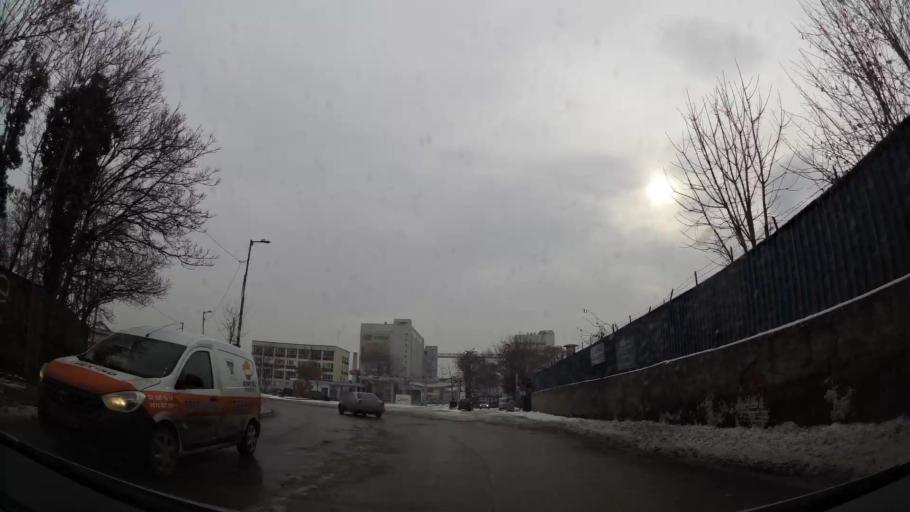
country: BG
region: Sofia-Capital
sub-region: Stolichna Obshtina
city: Sofia
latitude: 42.7069
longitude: 23.3368
